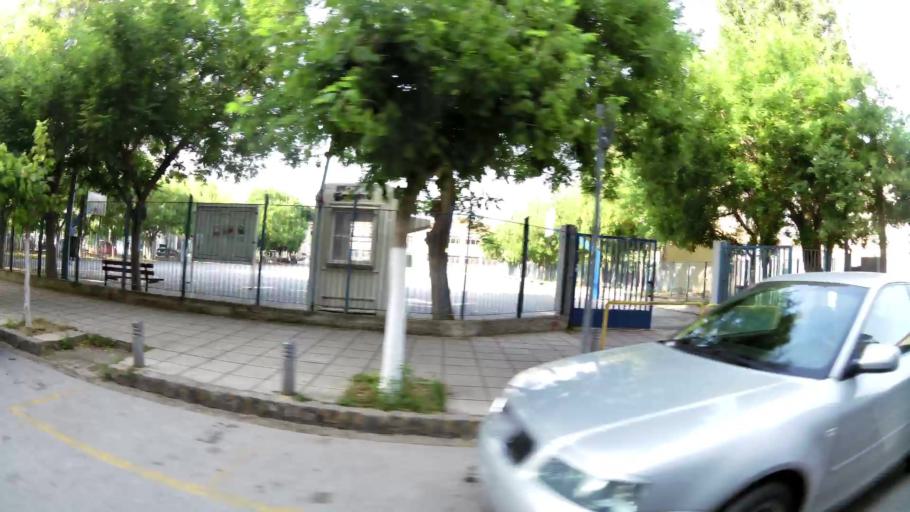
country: GR
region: Central Macedonia
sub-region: Nomos Thessalonikis
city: Menemeni
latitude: 40.6574
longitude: 22.9097
